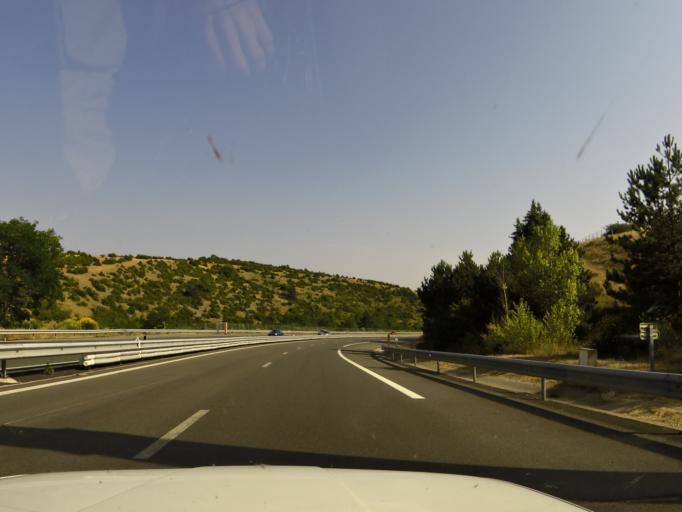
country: FR
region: Languedoc-Roussillon
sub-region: Departement de l'Herault
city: Lodeve
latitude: 43.8433
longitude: 3.3124
